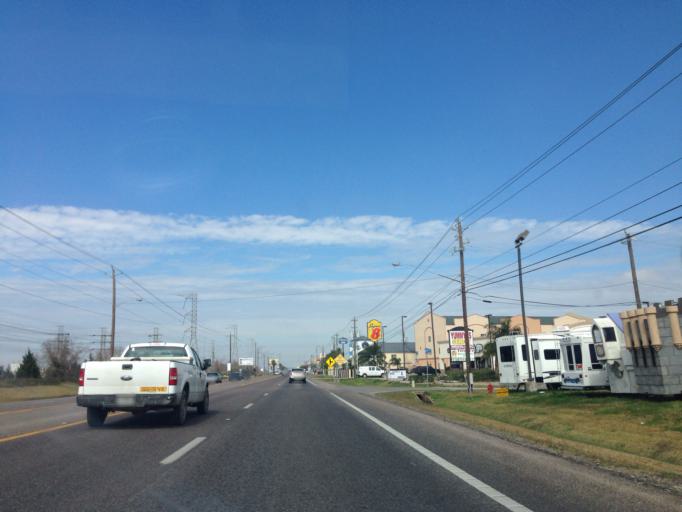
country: US
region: Texas
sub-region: Galveston County
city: Kemah
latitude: 29.5319
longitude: -95.0145
